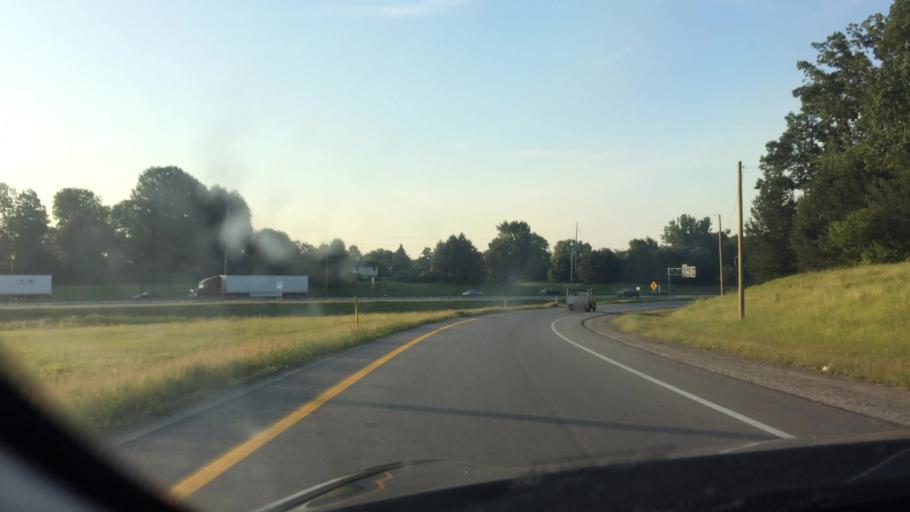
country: US
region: Ohio
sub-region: Lucas County
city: Holland
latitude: 41.6109
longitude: -83.6928
